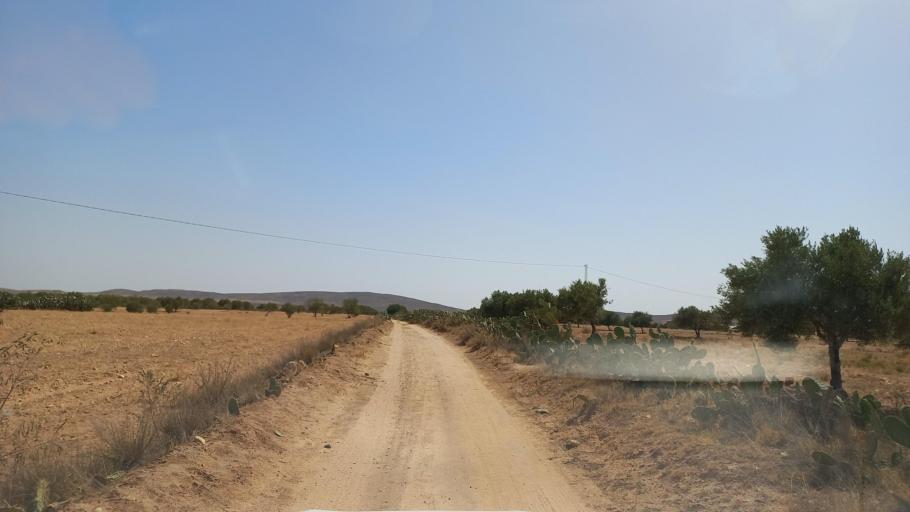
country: TN
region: Al Qasrayn
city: Kasserine
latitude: 35.2196
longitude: 9.0362
